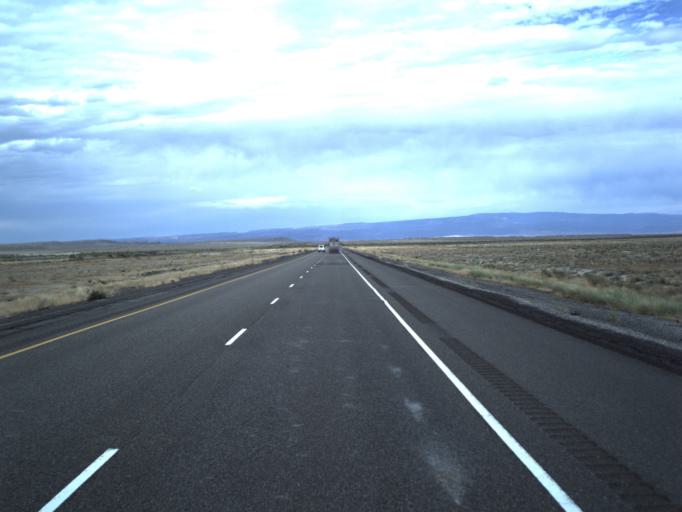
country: US
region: Utah
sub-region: Grand County
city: Moab
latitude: 38.9418
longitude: -109.5838
